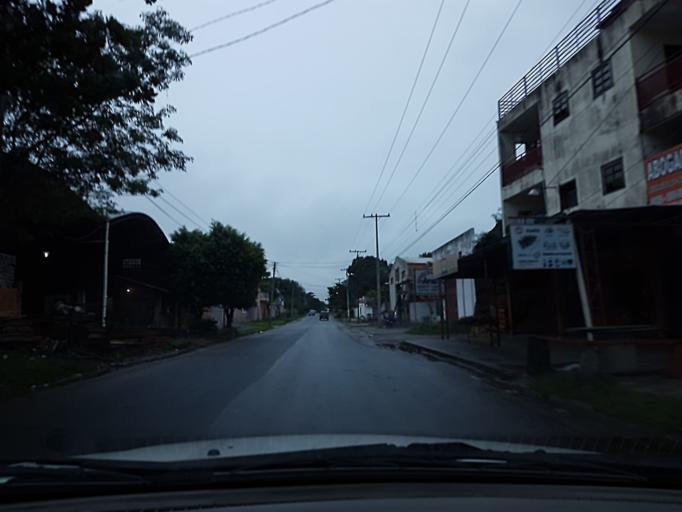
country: PY
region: Central
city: Colonia Mariano Roque Alonso
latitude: -25.2178
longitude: -57.5379
